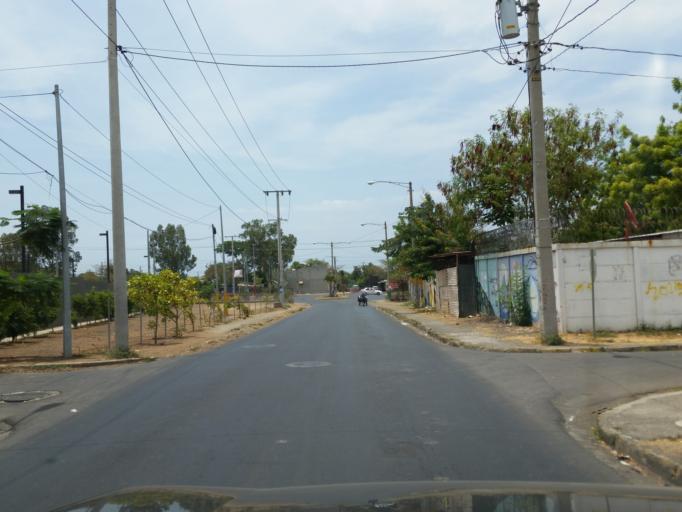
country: NI
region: Managua
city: Managua
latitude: 12.1527
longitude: -86.2680
